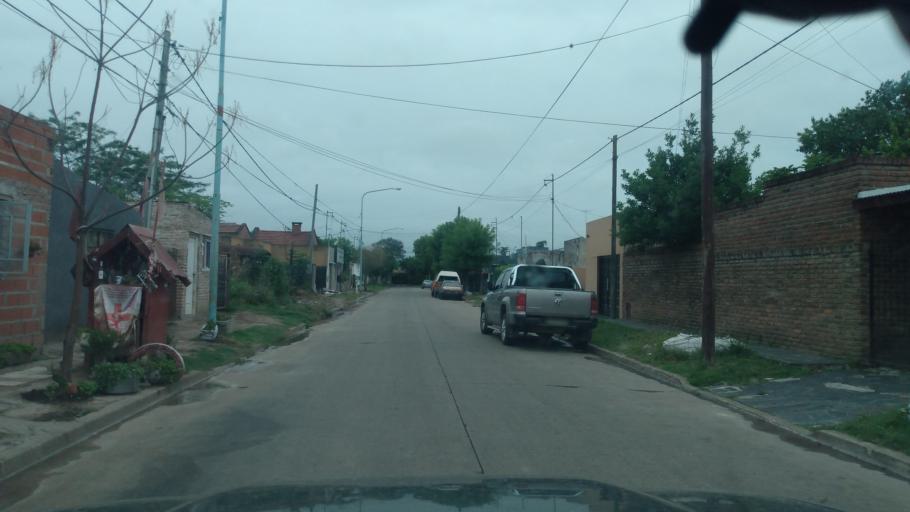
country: AR
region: Buenos Aires
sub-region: Partido de Lujan
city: Lujan
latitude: -34.5758
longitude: -59.1189
